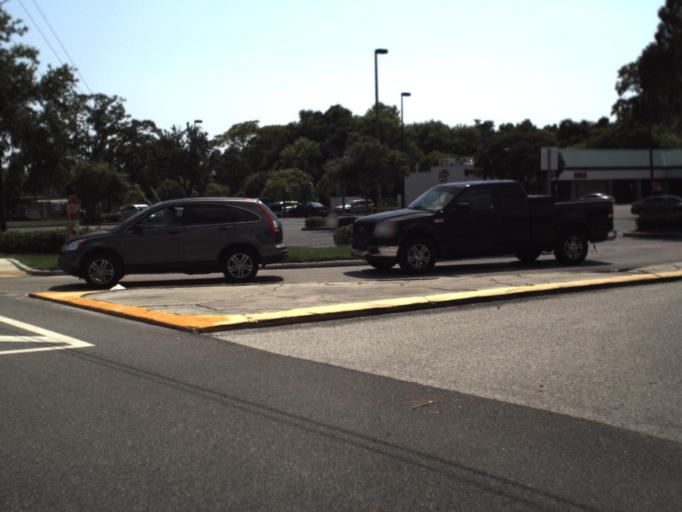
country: US
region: Florida
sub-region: Pinellas County
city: Kenneth City
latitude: 27.8121
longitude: -82.7287
